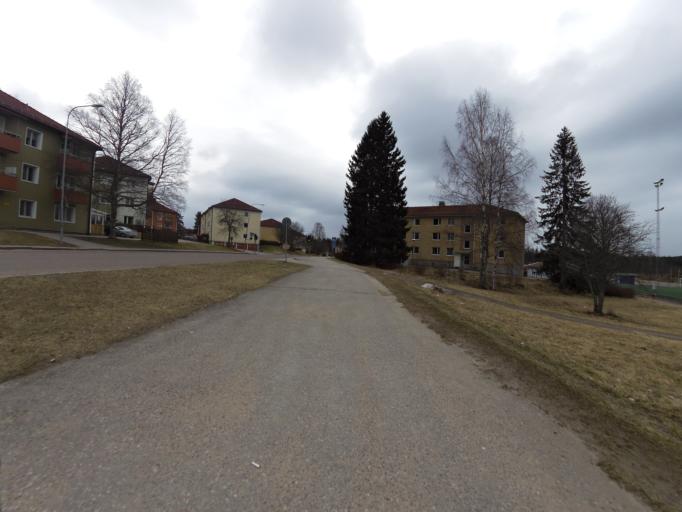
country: SE
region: Gaevleborg
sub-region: Hofors Kommun
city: Hofors
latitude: 60.5454
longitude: 16.2700
